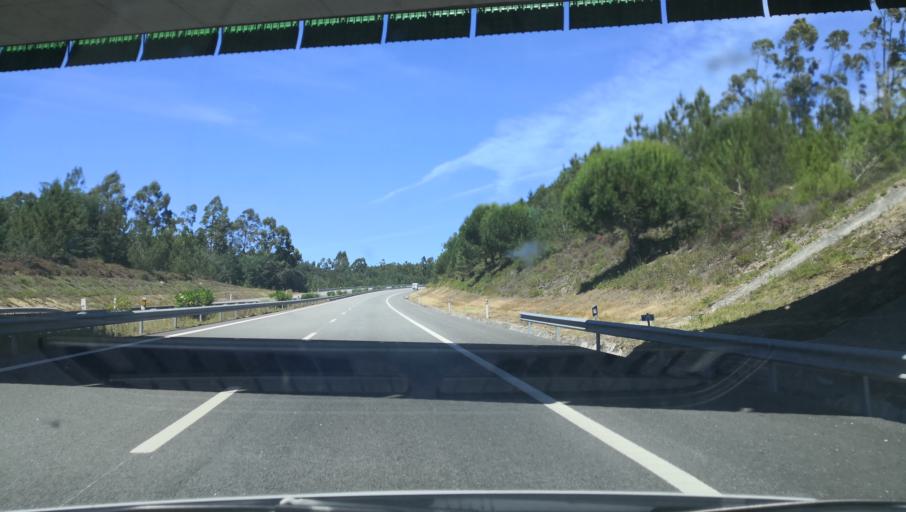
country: PT
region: Coimbra
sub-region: Montemor-O-Velho
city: Arazede
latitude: 40.2434
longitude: -8.6581
